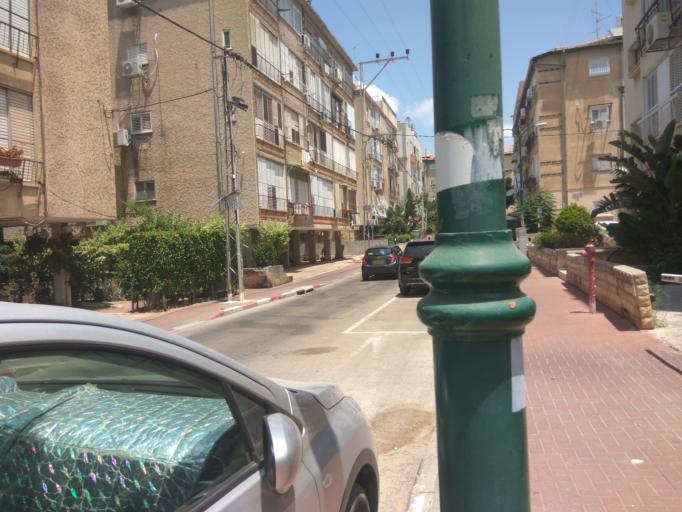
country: IL
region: Central District
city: Rishon LeZiyyon
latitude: 31.9625
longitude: 34.8057
